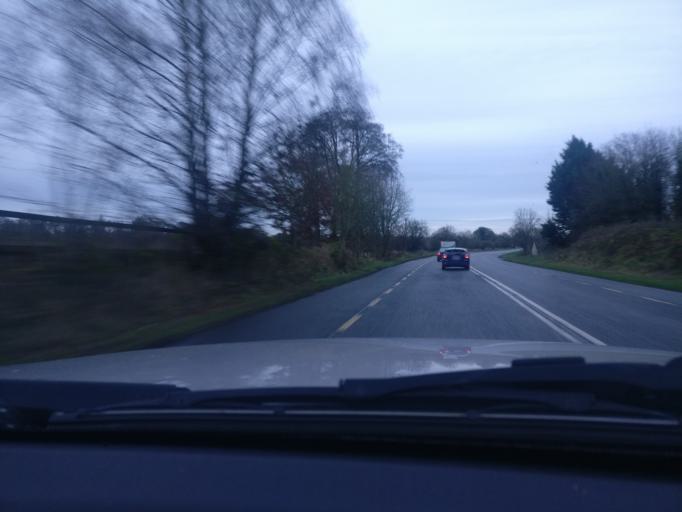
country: IE
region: Leinster
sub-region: An Mhi
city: Kells
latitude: 53.7100
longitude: -6.8070
